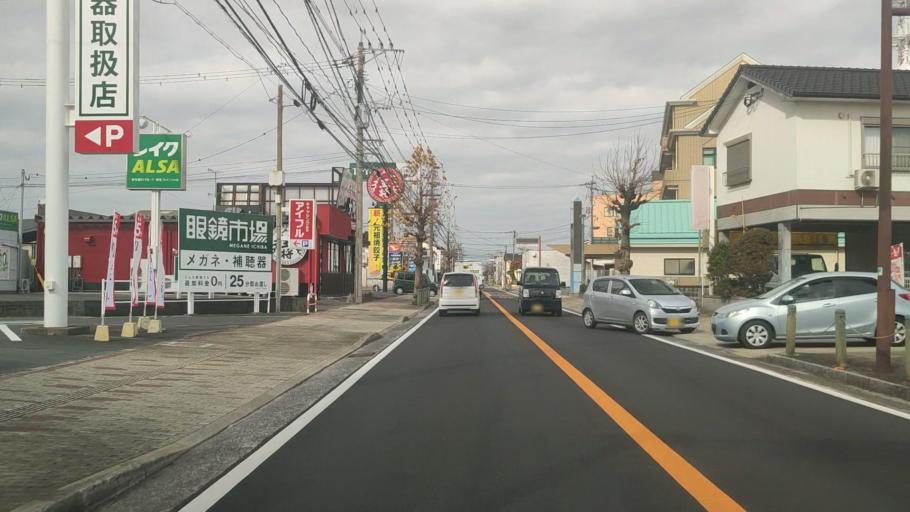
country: JP
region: Nagasaki
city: Shimabara
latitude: 32.7970
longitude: 130.3670
